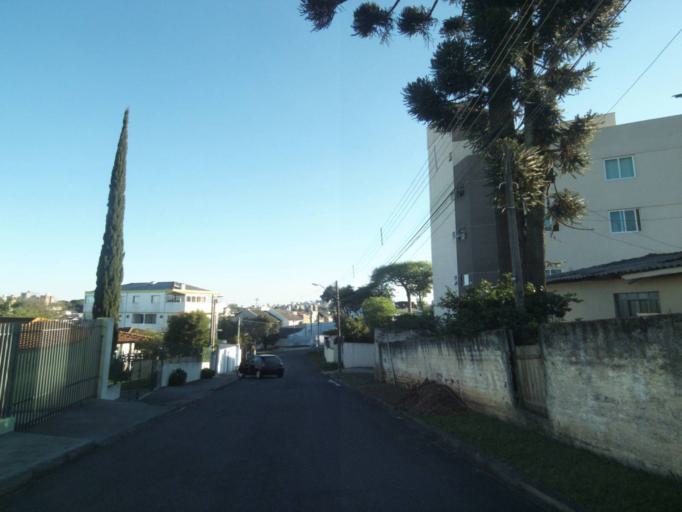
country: BR
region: Parana
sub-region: Curitiba
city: Curitiba
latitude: -25.3904
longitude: -49.2512
